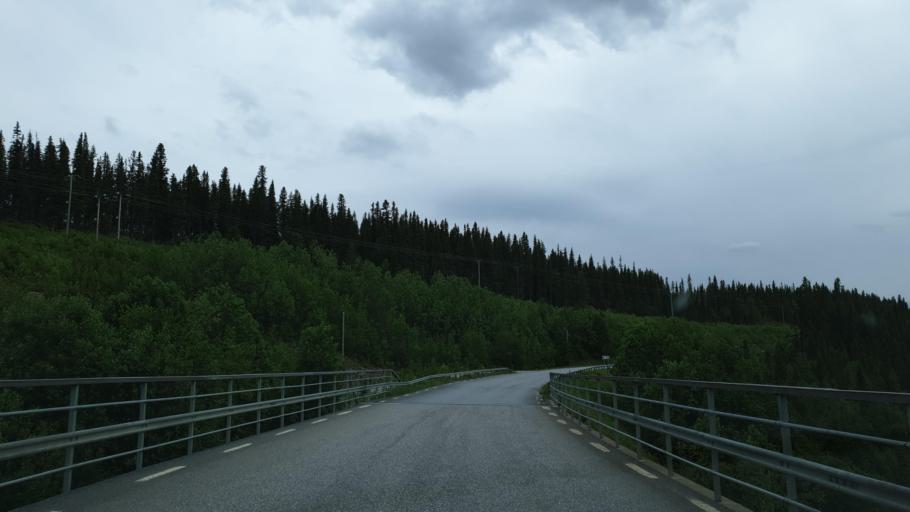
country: SE
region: Vaesterbotten
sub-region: Storumans Kommun
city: Fristad
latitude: 65.4236
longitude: 16.1717
